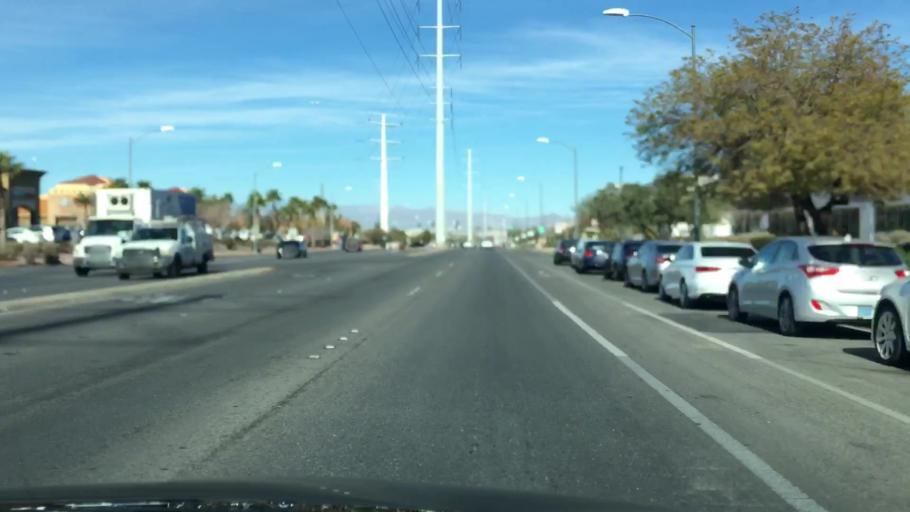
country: US
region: Nevada
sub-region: Clark County
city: Henderson
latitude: 36.0396
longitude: -115.0293
